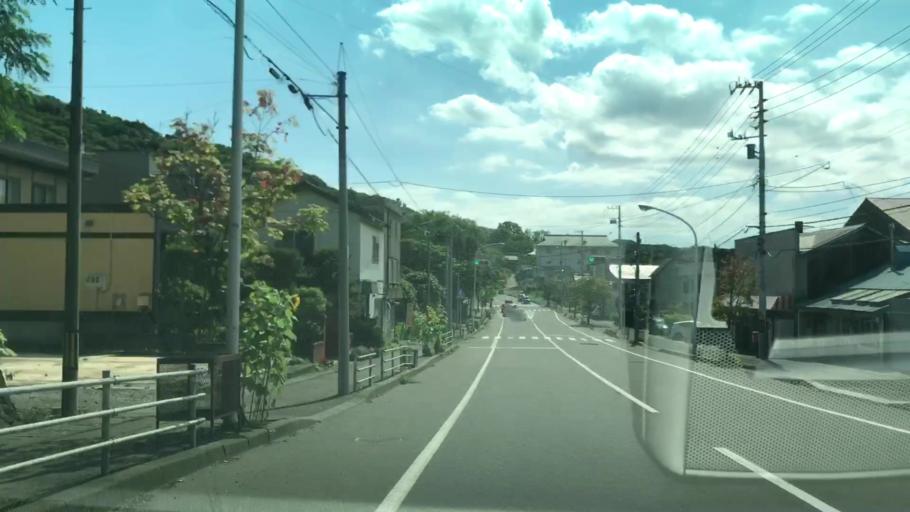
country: JP
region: Hokkaido
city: Muroran
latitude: 42.3207
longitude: 140.9969
